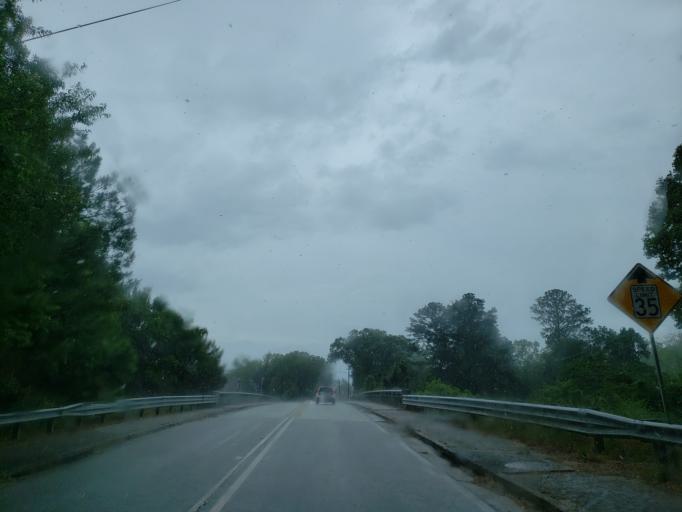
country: US
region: Georgia
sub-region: Haralson County
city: Buchanan
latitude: 33.8064
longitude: -85.1904
